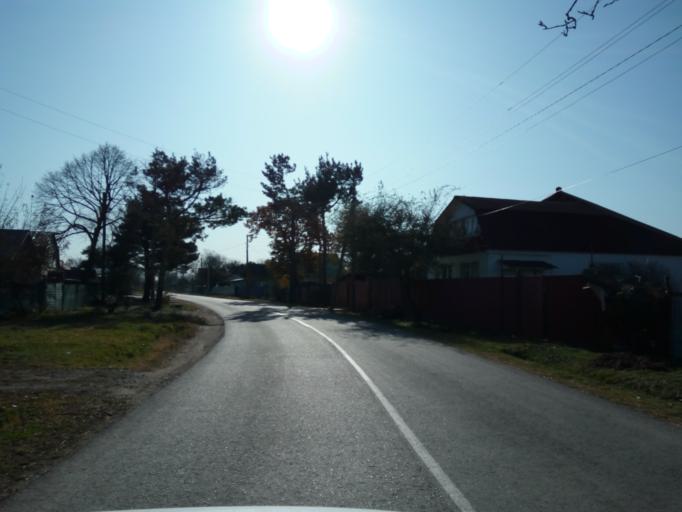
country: RU
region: Primorskiy
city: Dal'nerechensk
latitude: 45.9371
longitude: 133.7036
